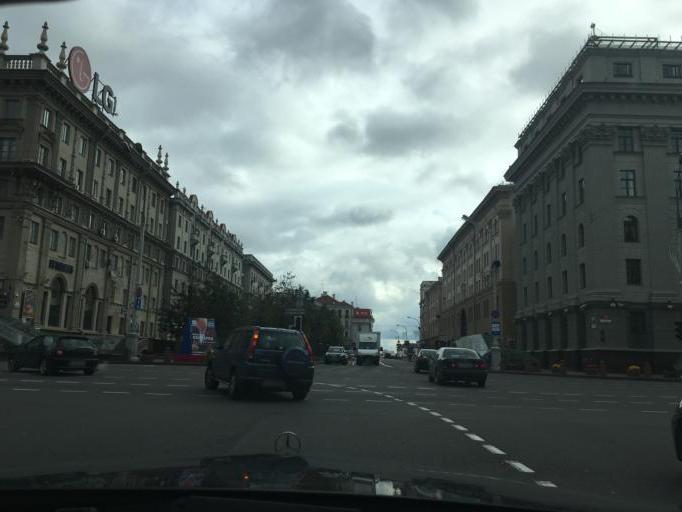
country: BY
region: Minsk
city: Minsk
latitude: 53.9007
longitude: 27.5588
